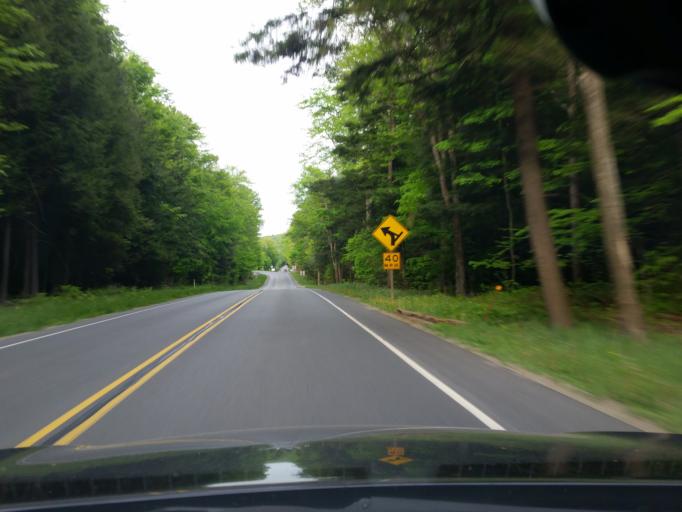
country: US
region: Pennsylvania
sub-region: McKean County
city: Kane
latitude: 41.5705
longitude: -78.8878
